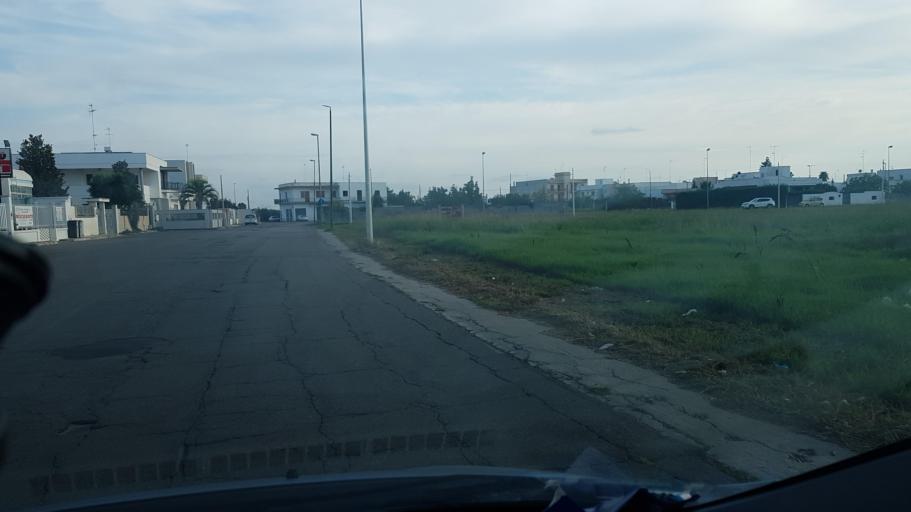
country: IT
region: Apulia
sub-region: Provincia di Lecce
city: Veglie
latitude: 40.3339
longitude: 17.9742
